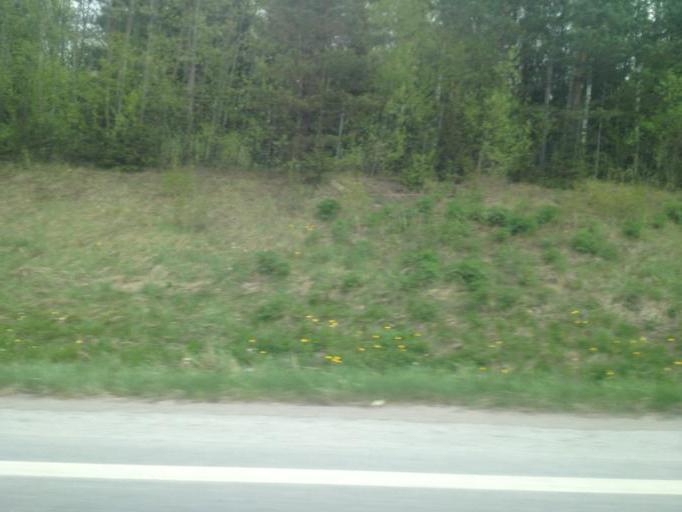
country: FI
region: Uusimaa
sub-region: Helsinki
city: Nurmijaervi
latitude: 60.3573
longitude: 24.8086
